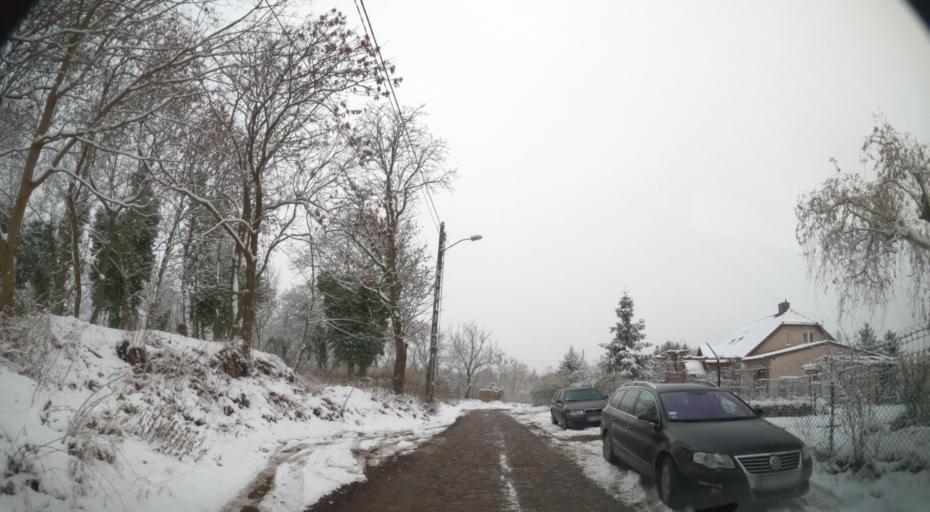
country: PL
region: West Pomeranian Voivodeship
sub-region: Szczecin
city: Szczecin
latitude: 53.3433
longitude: 14.5655
